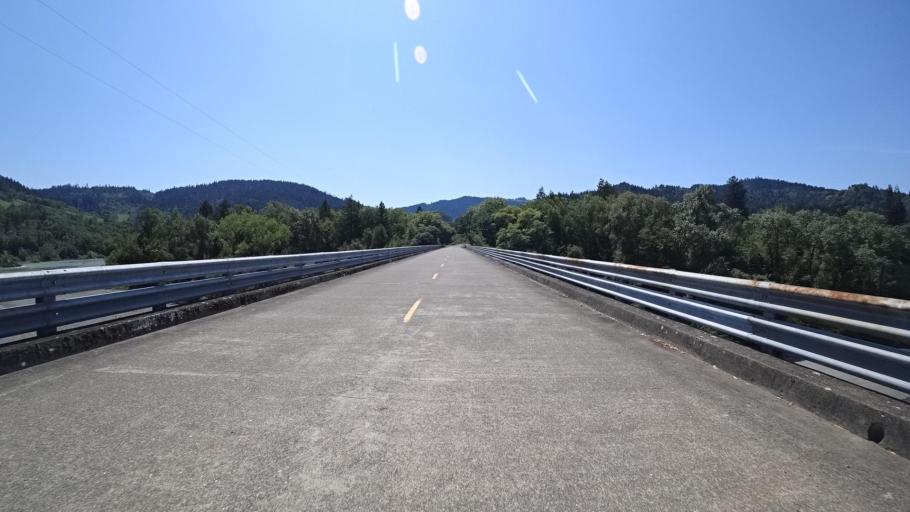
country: US
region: California
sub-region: Humboldt County
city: Redway
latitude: 40.2178
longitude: -123.6326
